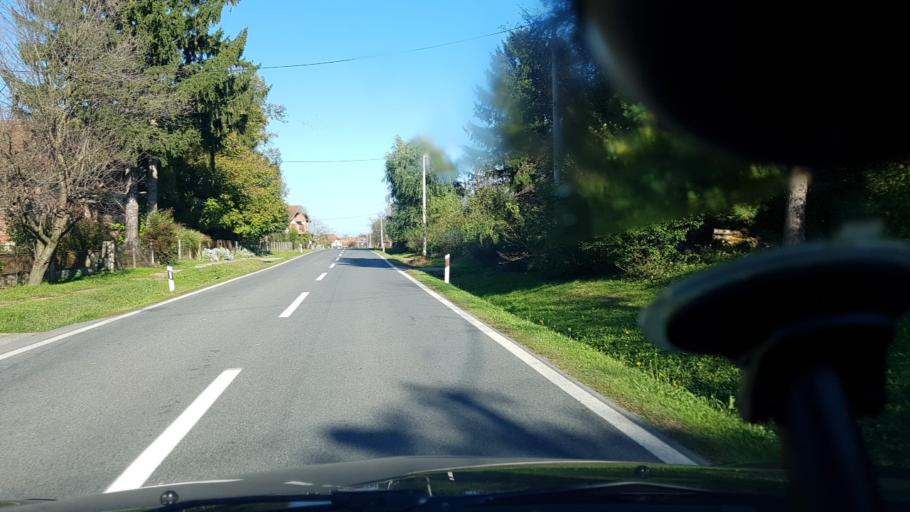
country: HR
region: Bjelovarsko-Bilogorska
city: Gudovac
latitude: 45.8322
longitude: 16.7690
